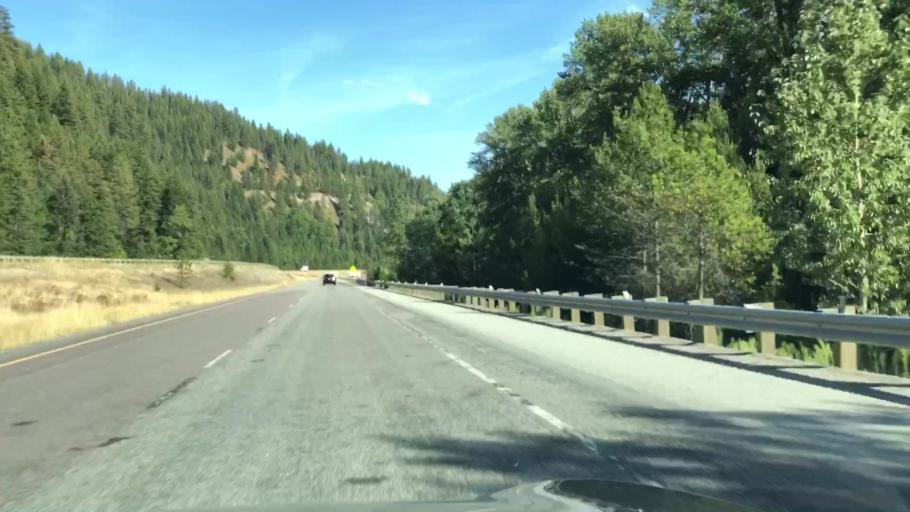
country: US
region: Montana
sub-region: Sanders County
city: Thompson Falls
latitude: 47.4046
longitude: -115.4841
